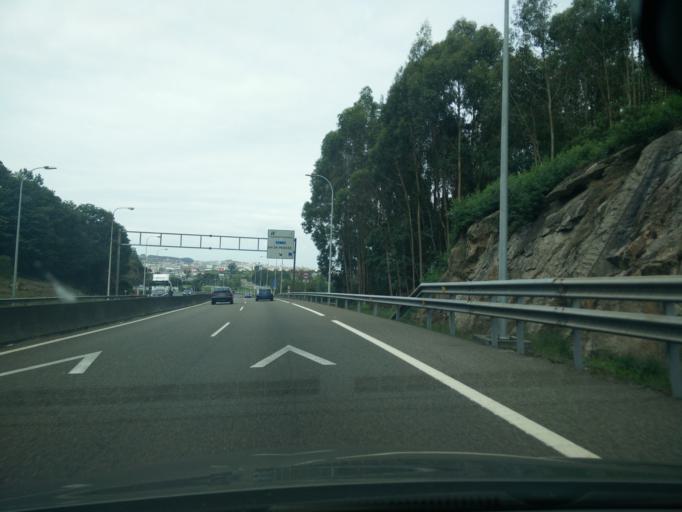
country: ES
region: Galicia
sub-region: Provincia da Coruna
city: Culleredo
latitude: 43.3249
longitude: -8.3935
